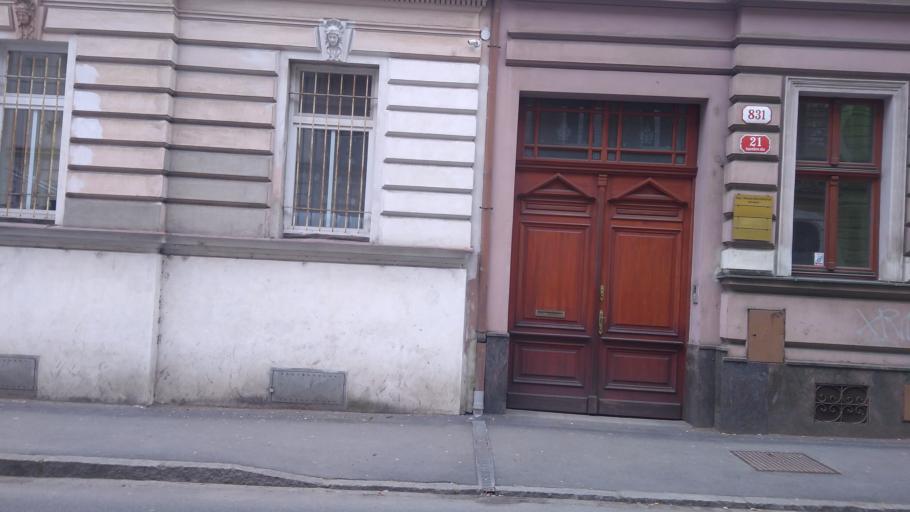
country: CZ
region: Plzensky
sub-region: Okres Plzen-Mesto
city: Pilsen
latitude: 49.7441
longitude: 13.3677
